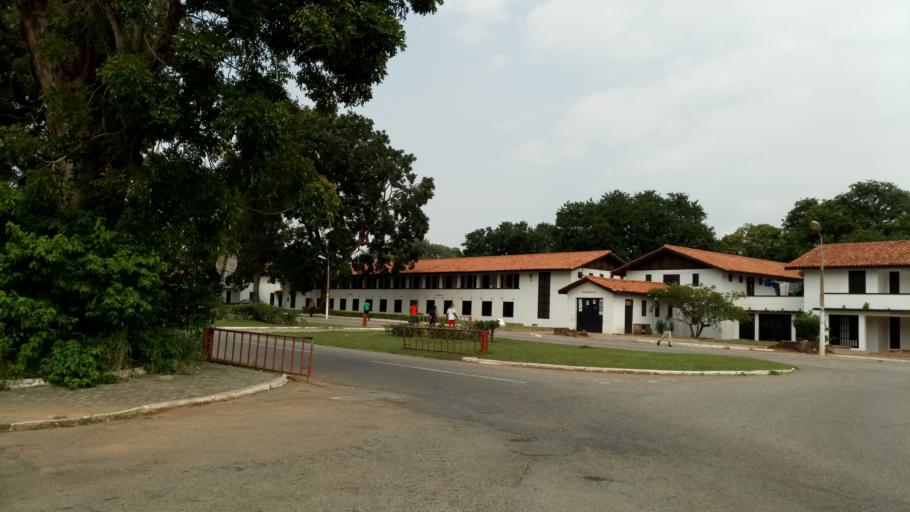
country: GH
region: Greater Accra
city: Medina Estates
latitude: 5.6508
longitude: -0.1869
